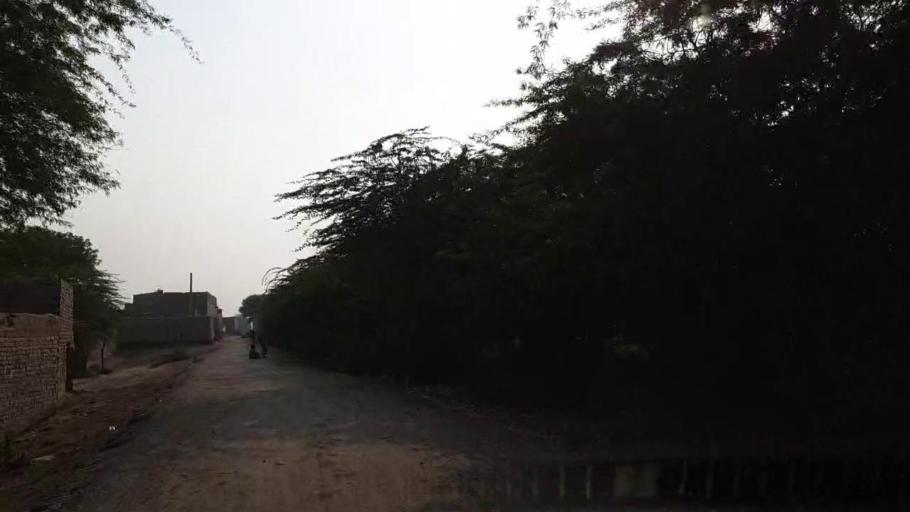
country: PK
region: Sindh
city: Bhan
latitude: 26.5609
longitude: 67.7037
